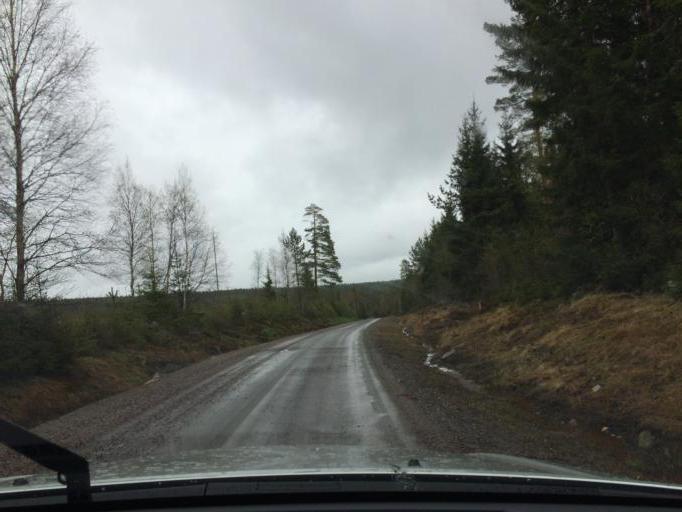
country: SE
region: Dalarna
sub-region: Ludvika Kommun
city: Abborrberget
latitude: 60.0384
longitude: 14.6542
